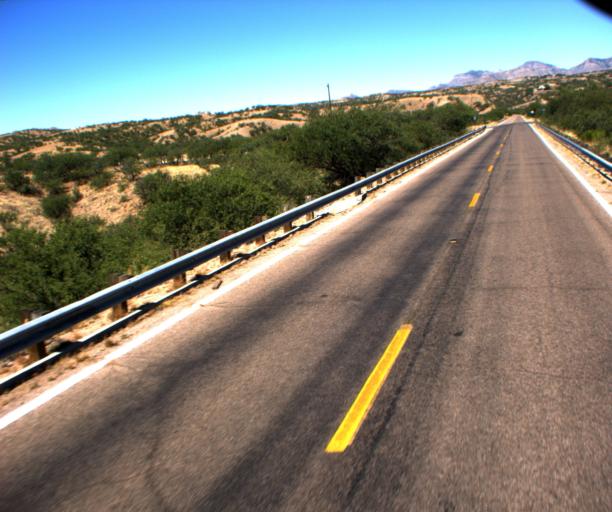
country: US
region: Arizona
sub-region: Santa Cruz County
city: Rio Rico
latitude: 31.4297
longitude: -110.9953
